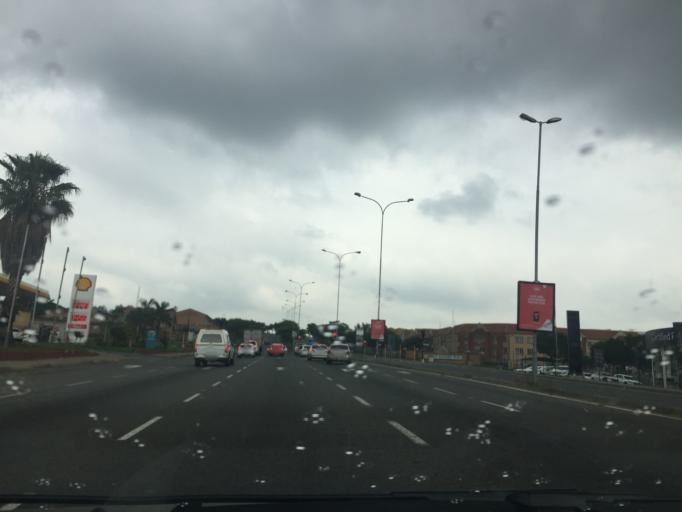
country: ZA
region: Gauteng
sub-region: City of Johannesburg Metropolitan Municipality
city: Modderfontein
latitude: -26.0902
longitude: 28.0921
